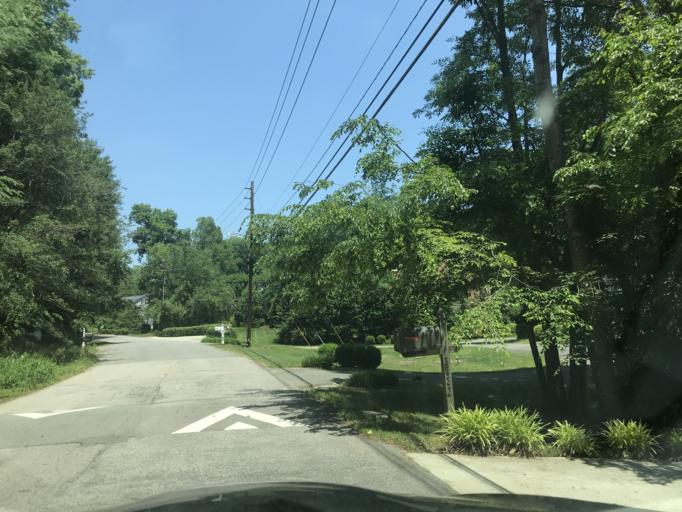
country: US
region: North Carolina
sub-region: Wake County
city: West Raleigh
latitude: 35.8300
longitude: -78.6562
